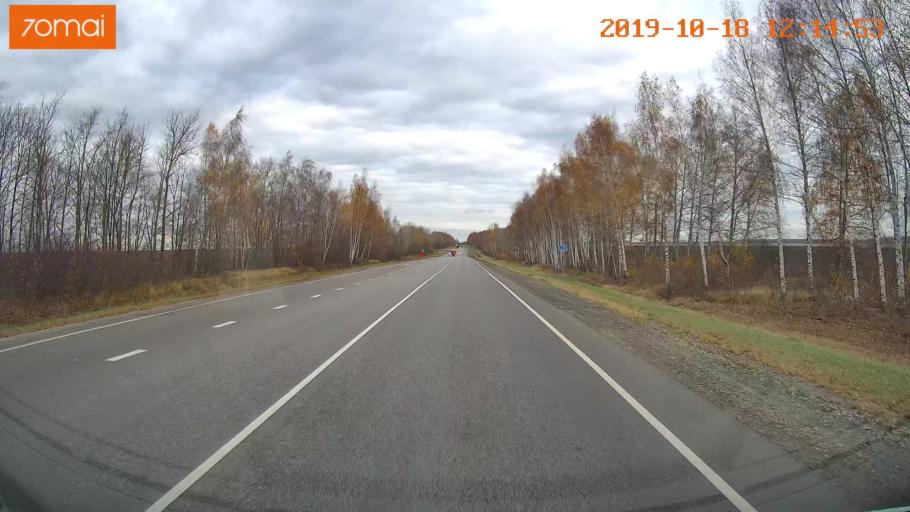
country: RU
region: Rjazan
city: Zakharovo
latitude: 54.4364
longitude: 39.3907
